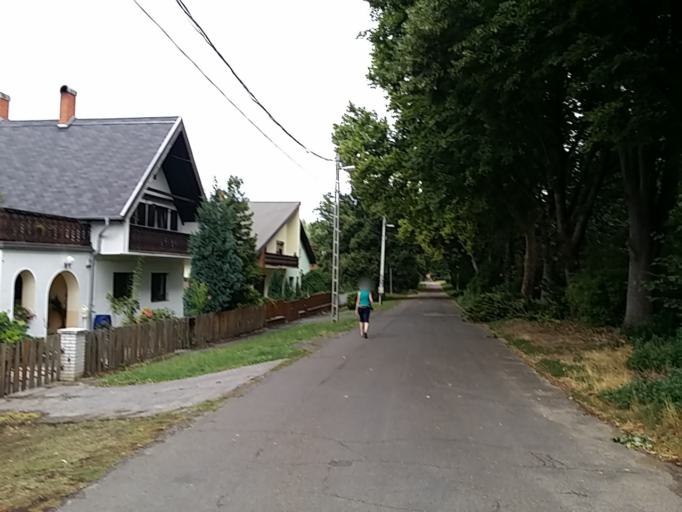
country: HU
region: Somogy
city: Balatonboglar
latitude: 46.7735
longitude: 17.6563
